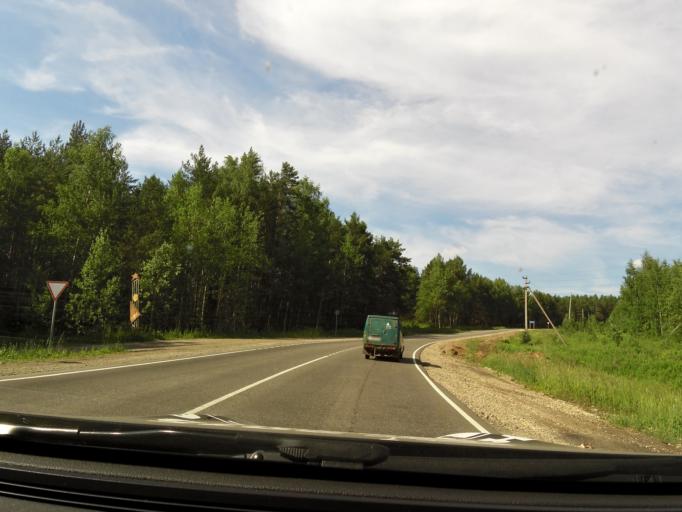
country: RU
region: Kirov
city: Belaya Kholunitsa
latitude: 58.8379
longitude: 50.6868
